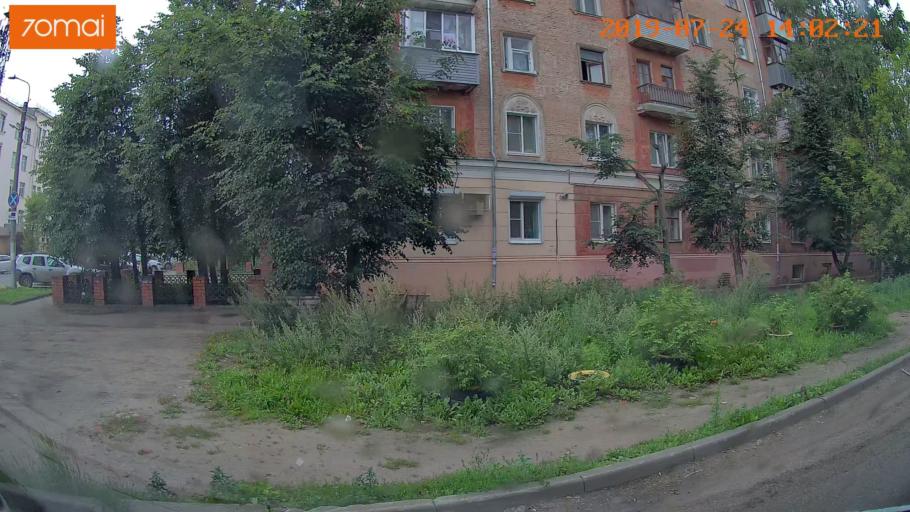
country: RU
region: Ivanovo
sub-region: Gorod Ivanovo
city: Ivanovo
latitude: 57.0083
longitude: 40.9800
